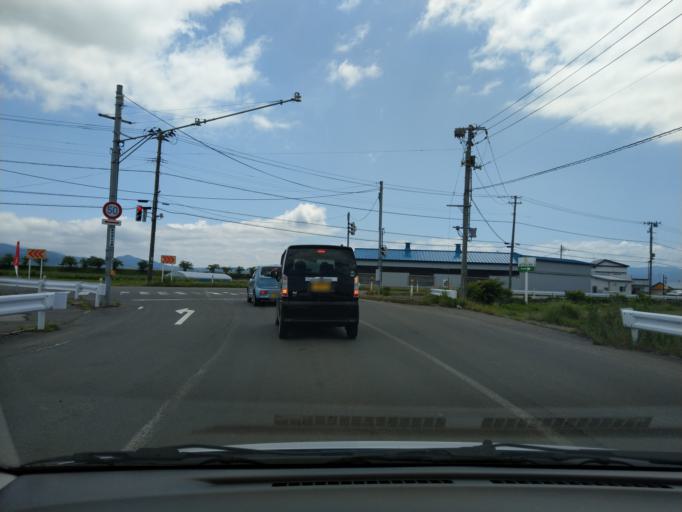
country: JP
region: Aomori
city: Kuroishi
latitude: 40.6367
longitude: 140.5675
